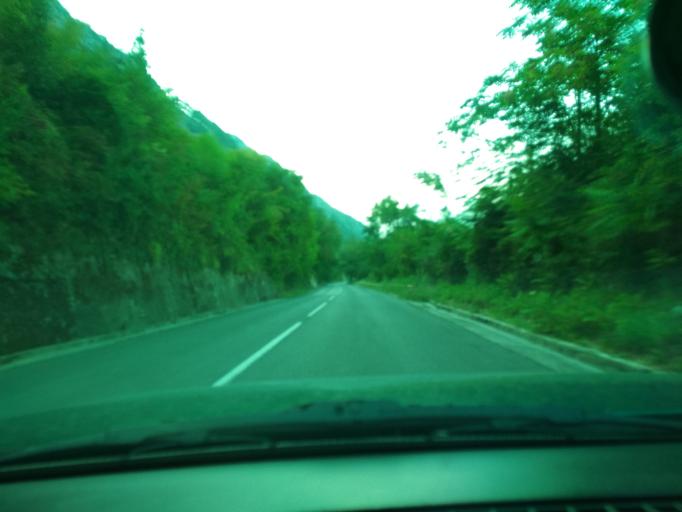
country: ME
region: Kotor
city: Kotor
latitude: 42.4146
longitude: 18.7612
